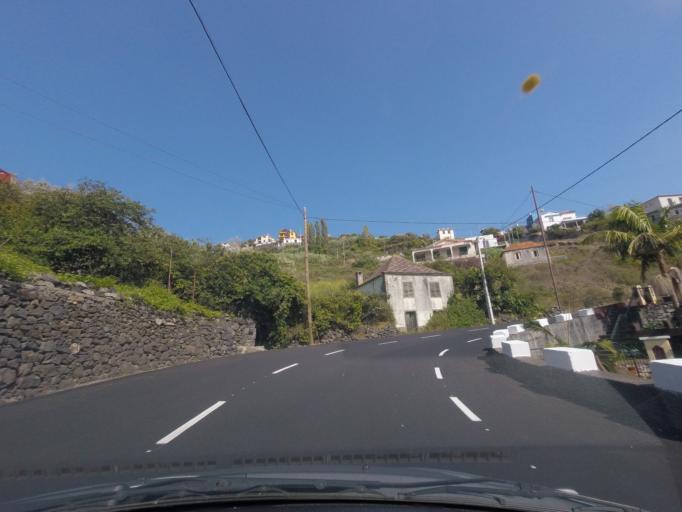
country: PT
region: Madeira
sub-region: Ribeira Brava
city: Campanario
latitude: 32.6695
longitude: -17.0529
